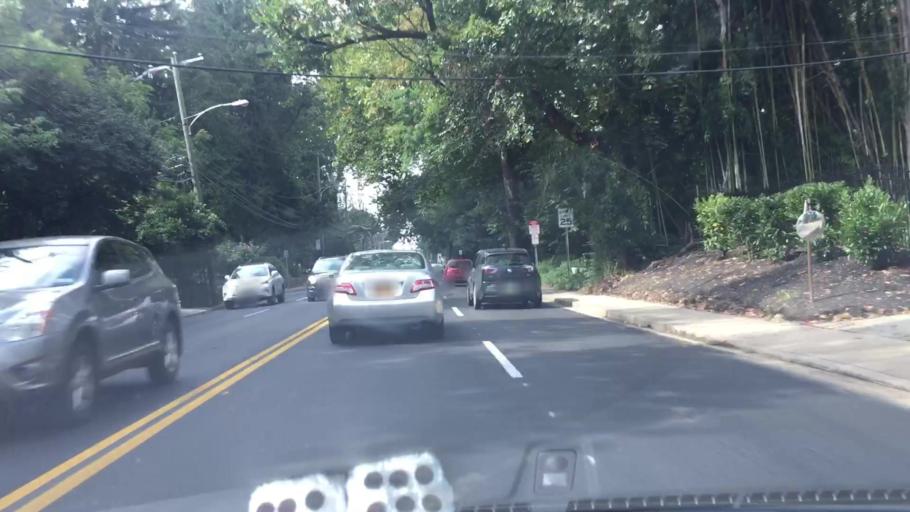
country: US
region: Pennsylvania
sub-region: Montgomery County
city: Bala-Cynwyd
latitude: 40.0068
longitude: -75.2470
